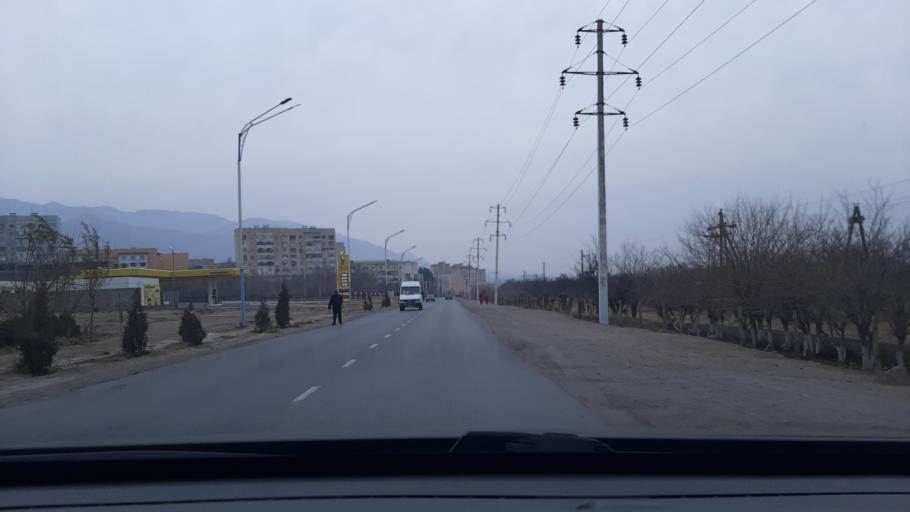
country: TJ
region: Viloyati Sughd
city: Khujand
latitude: 40.2833
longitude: 69.5878
